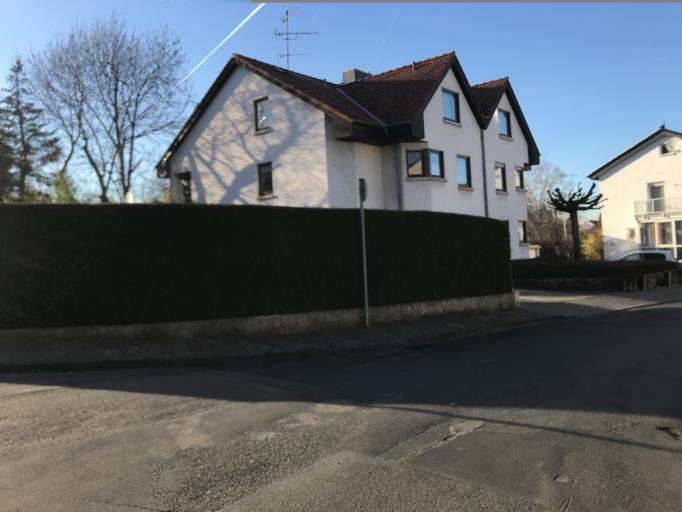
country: DE
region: Rheinland-Pfalz
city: Klein-Winternheim
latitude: 49.9580
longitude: 8.2266
